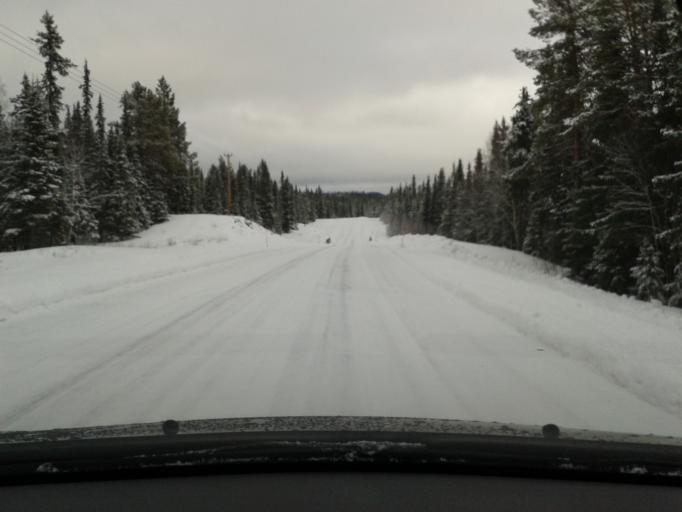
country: SE
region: Vaesterbotten
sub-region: Vilhelmina Kommun
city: Sjoberg
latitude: 65.2381
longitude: 15.7989
